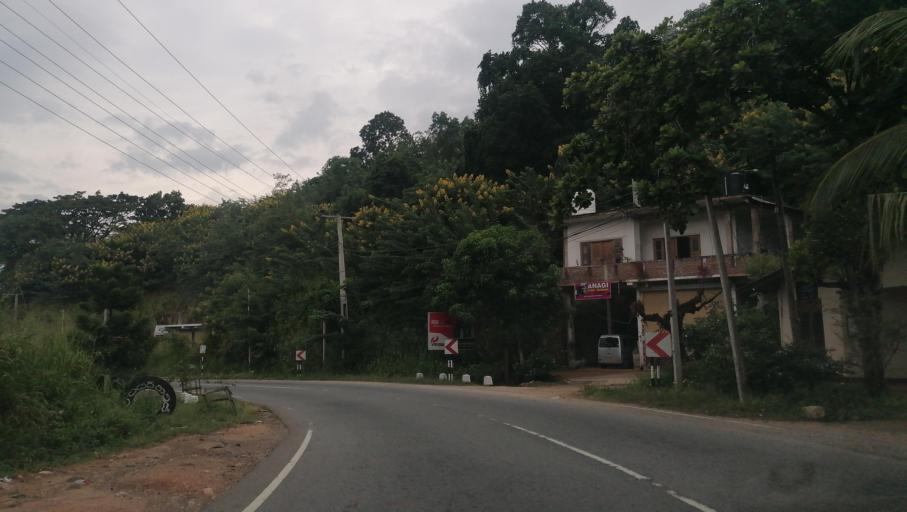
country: LK
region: Central
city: Kandy
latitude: 7.2481
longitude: 80.7304
